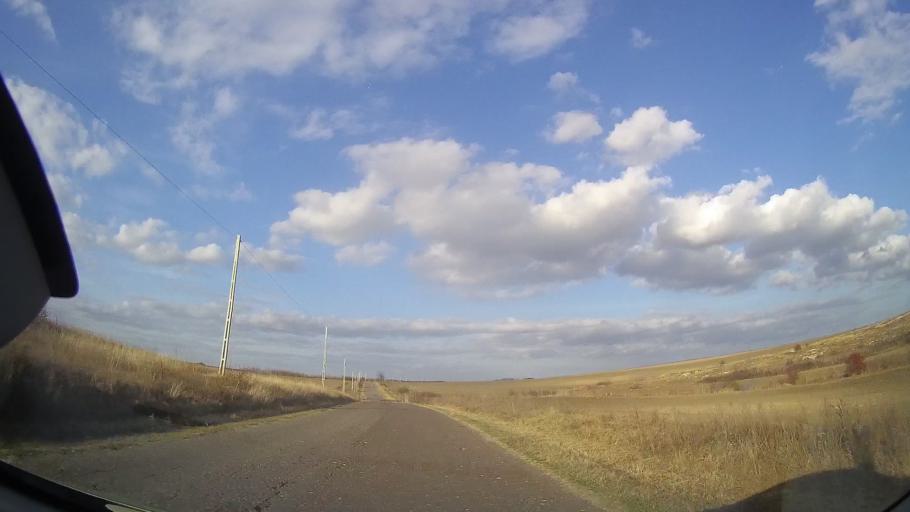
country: RO
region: Constanta
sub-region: Comuna Cerchezu
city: Cerchezu
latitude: 43.8422
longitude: 28.0984
